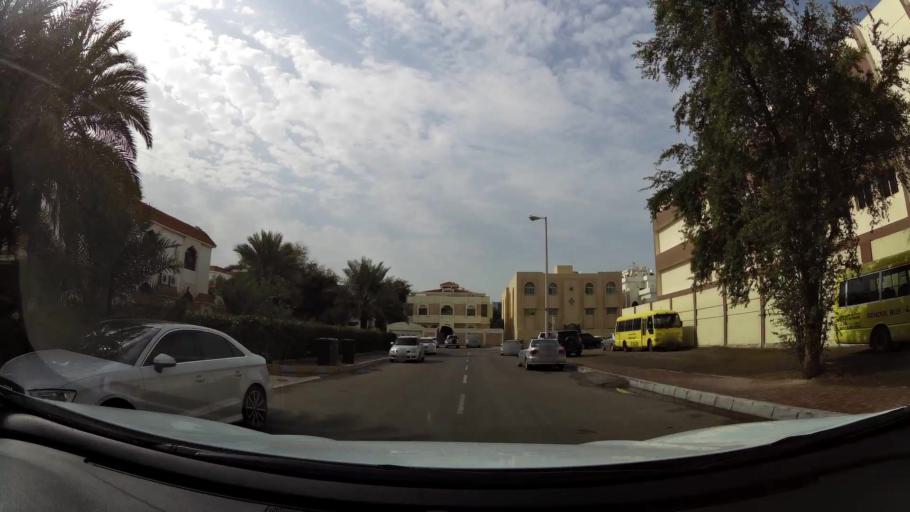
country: AE
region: Abu Dhabi
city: Abu Dhabi
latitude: 24.4444
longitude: 54.4114
